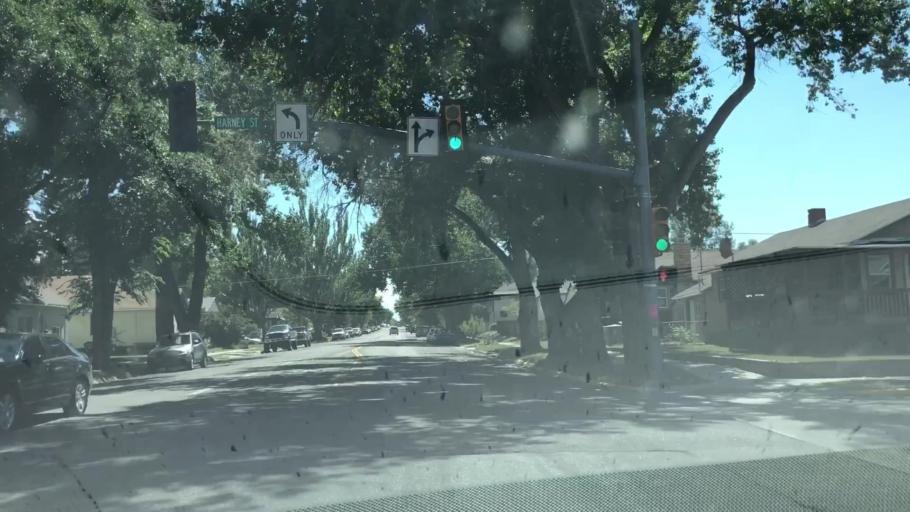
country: US
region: Wyoming
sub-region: Albany County
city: Laramie
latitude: 41.3190
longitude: -105.5849
